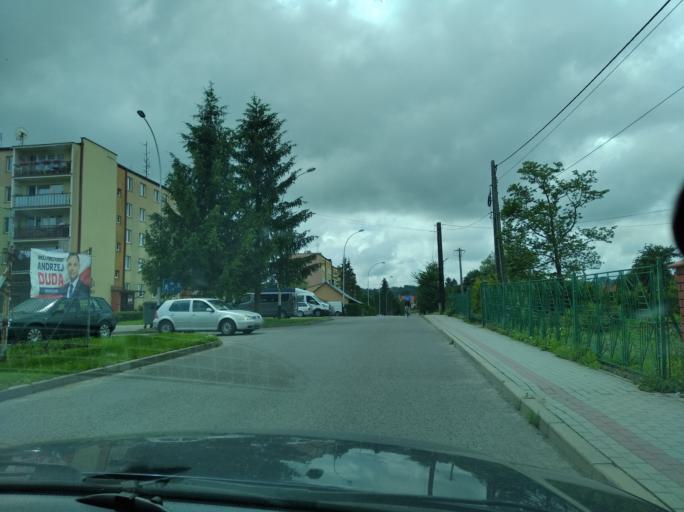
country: PL
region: Subcarpathian Voivodeship
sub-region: Powiat rzeszowski
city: Dynow
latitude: 49.8190
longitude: 22.2319
